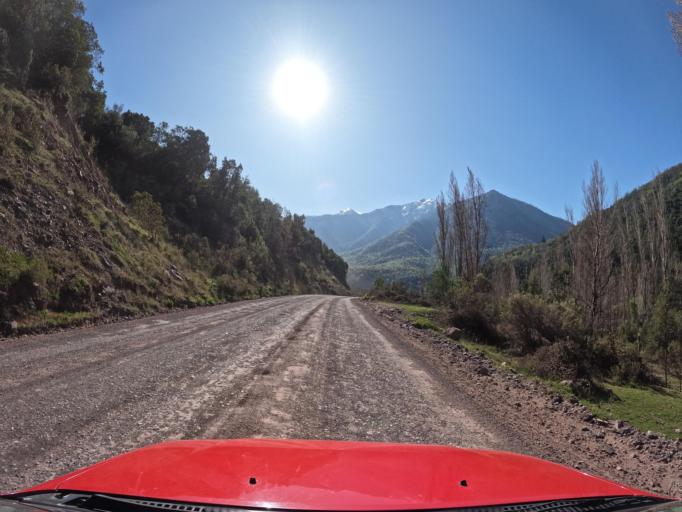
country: CL
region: O'Higgins
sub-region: Provincia de Colchagua
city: Chimbarongo
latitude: -35.0038
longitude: -70.7590
